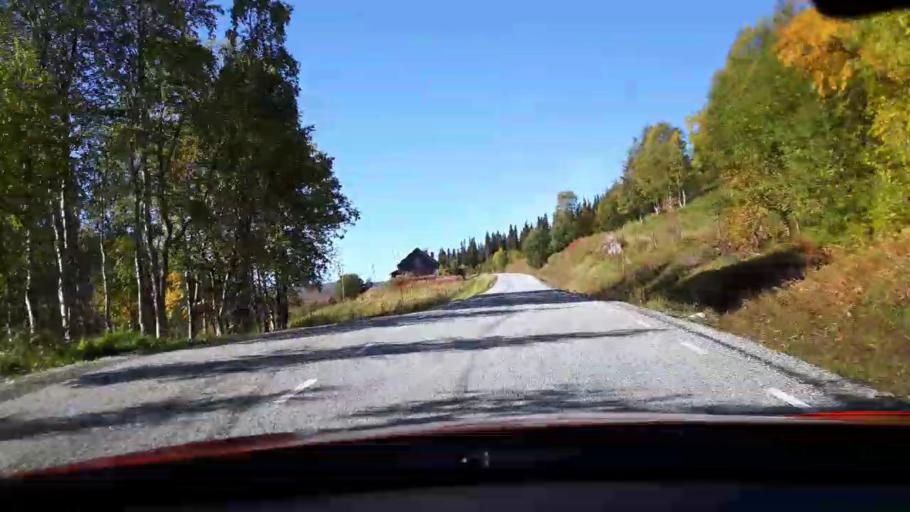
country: NO
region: Nord-Trondelag
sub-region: Royrvik
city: Royrvik
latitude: 64.8764
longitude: 14.2313
